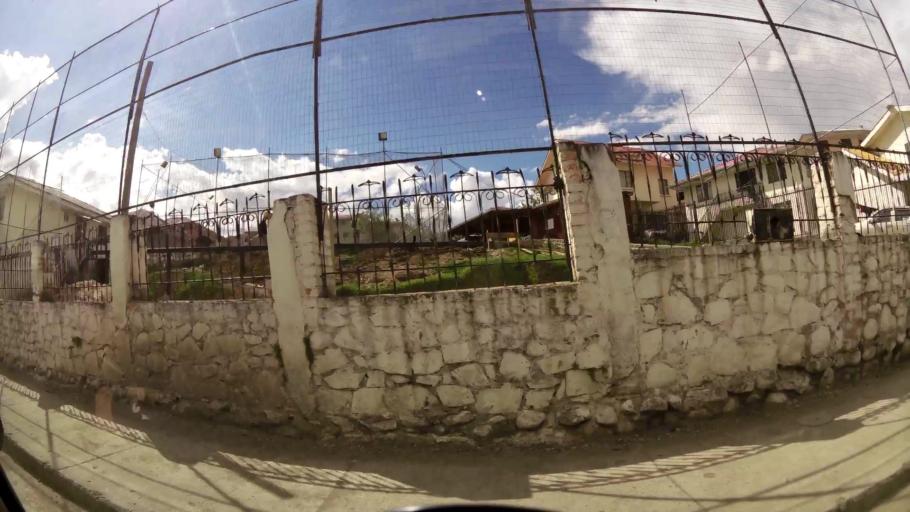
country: EC
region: Azuay
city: Cuenca
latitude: -2.8843
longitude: -78.9891
